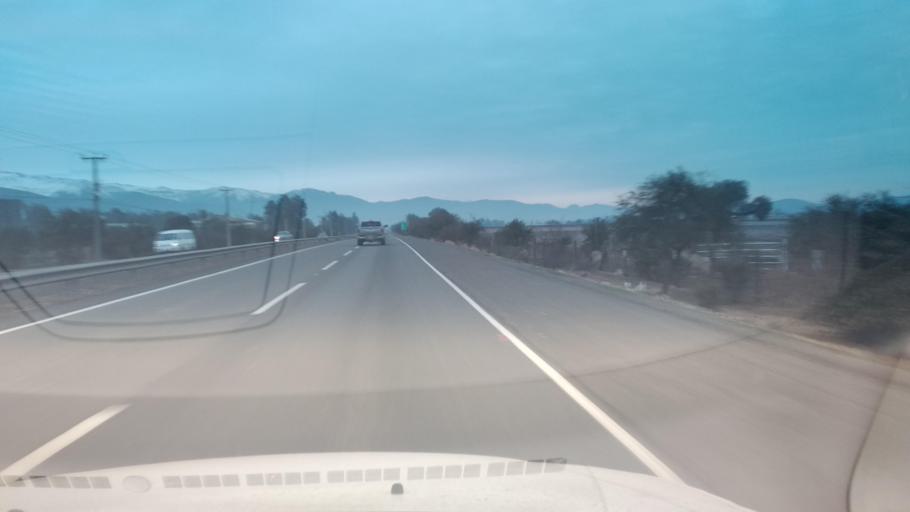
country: CL
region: Santiago Metropolitan
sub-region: Provincia de Chacabuco
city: Chicureo Abajo
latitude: -33.1336
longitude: -70.6682
